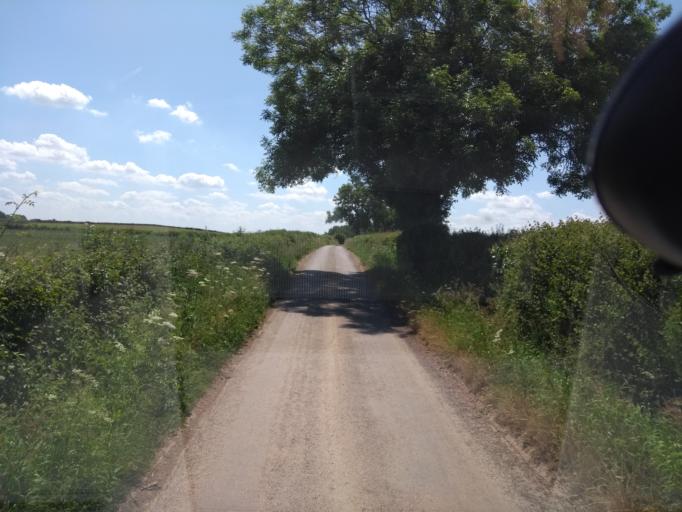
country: GB
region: England
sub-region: Somerset
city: North Petherton
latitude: 51.0552
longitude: -2.9995
